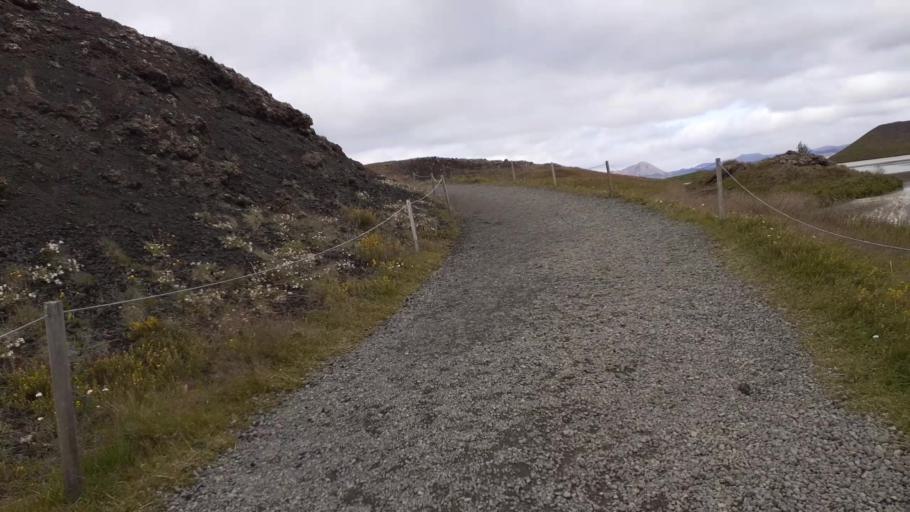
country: IS
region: Northeast
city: Laugar
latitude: 65.5677
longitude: -17.0338
